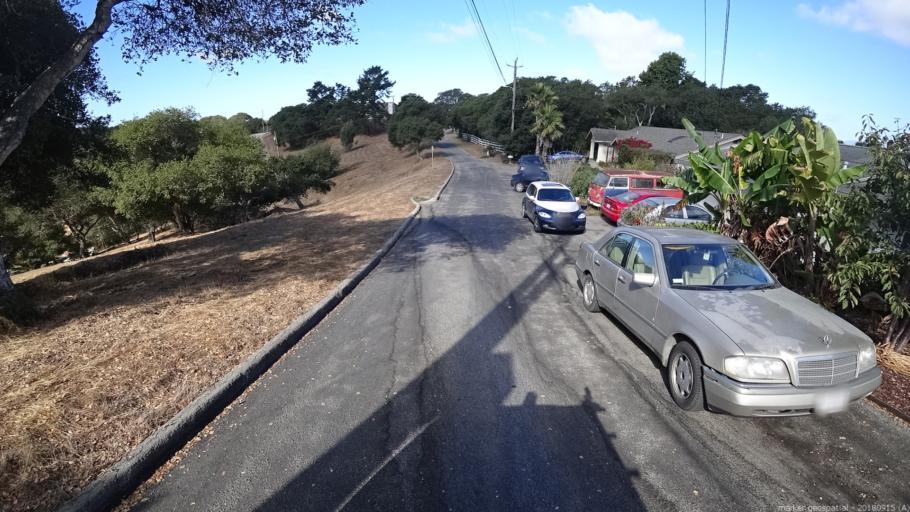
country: US
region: California
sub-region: Monterey County
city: Las Lomas
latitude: 36.8793
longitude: -121.7335
